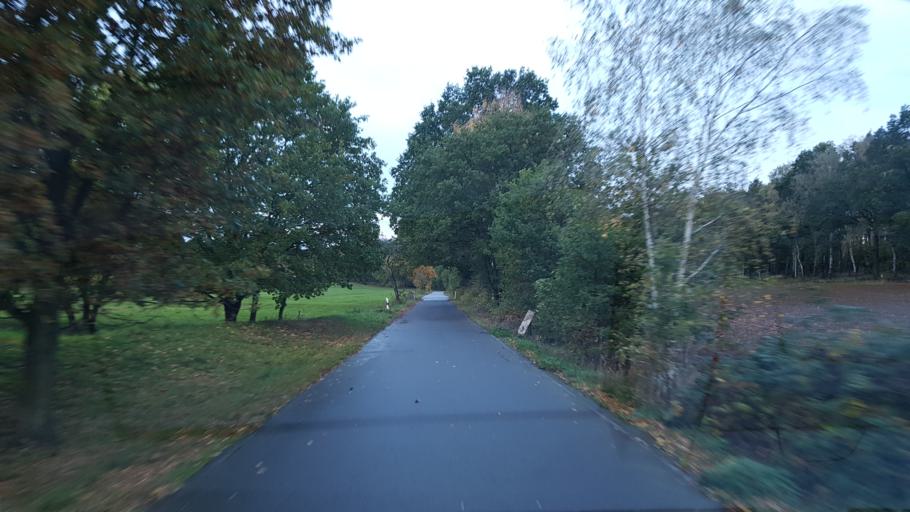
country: DE
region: Saxony
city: Cavertitz
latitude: 51.4205
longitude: 13.0857
